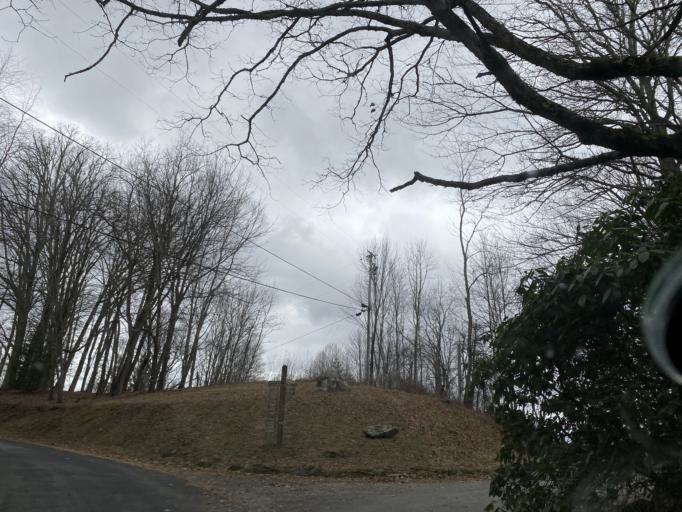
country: US
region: North Carolina
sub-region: Jackson County
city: Cullowhee
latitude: 35.2182
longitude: -83.1762
